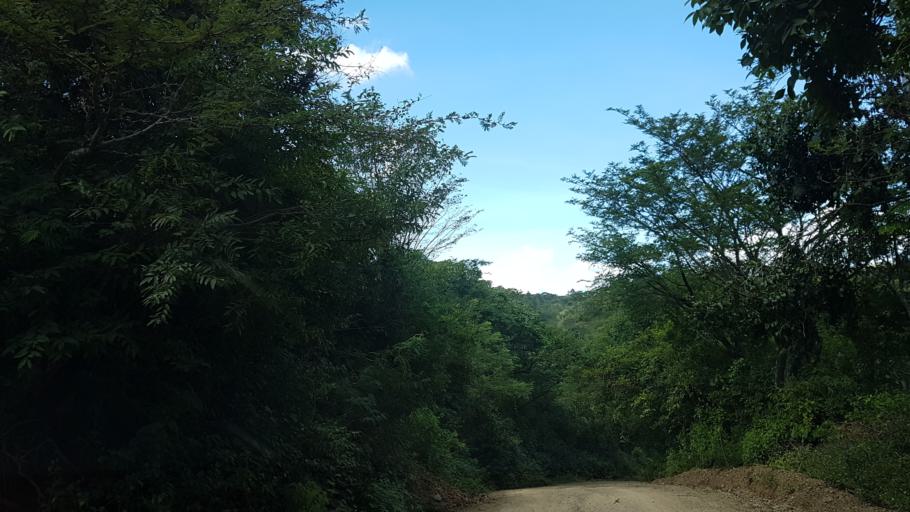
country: HN
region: El Paraiso
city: Oropoli
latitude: 13.7378
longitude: -86.6999
